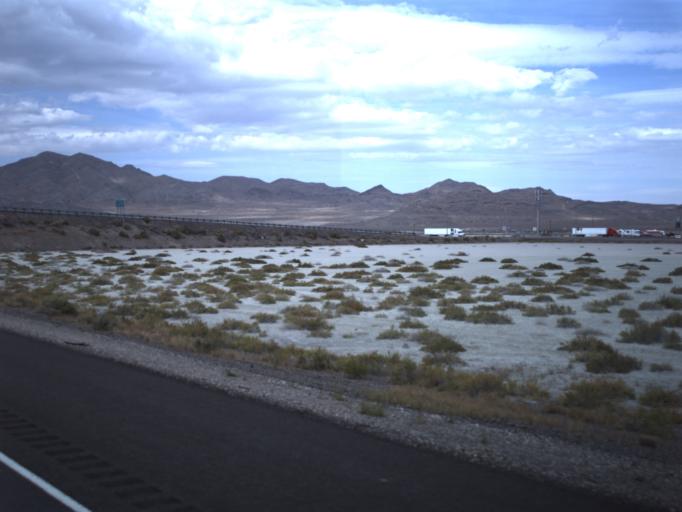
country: US
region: Utah
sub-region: Tooele County
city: Wendover
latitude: 40.7420
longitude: -113.9682
